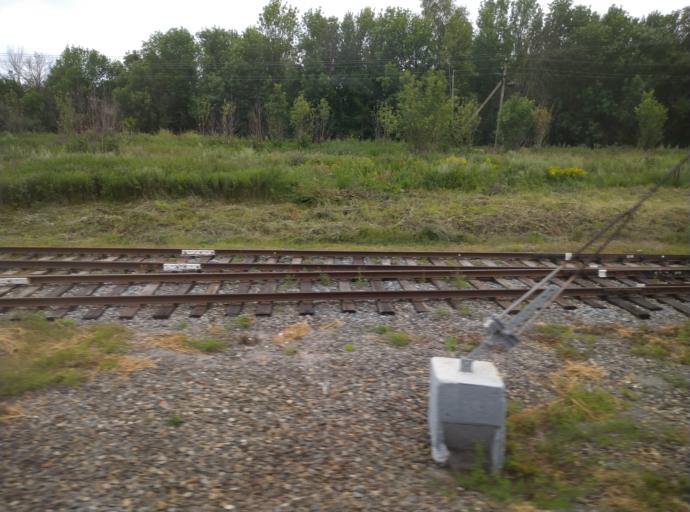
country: RU
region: Kostroma
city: Kosmynino
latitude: 57.5865
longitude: 40.7589
